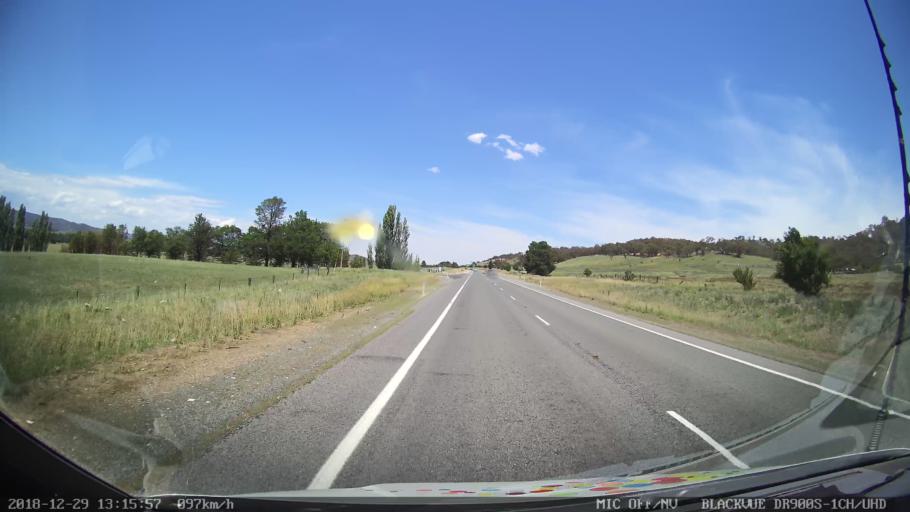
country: AU
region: Australian Capital Territory
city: Macarthur
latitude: -35.7162
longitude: 149.1593
